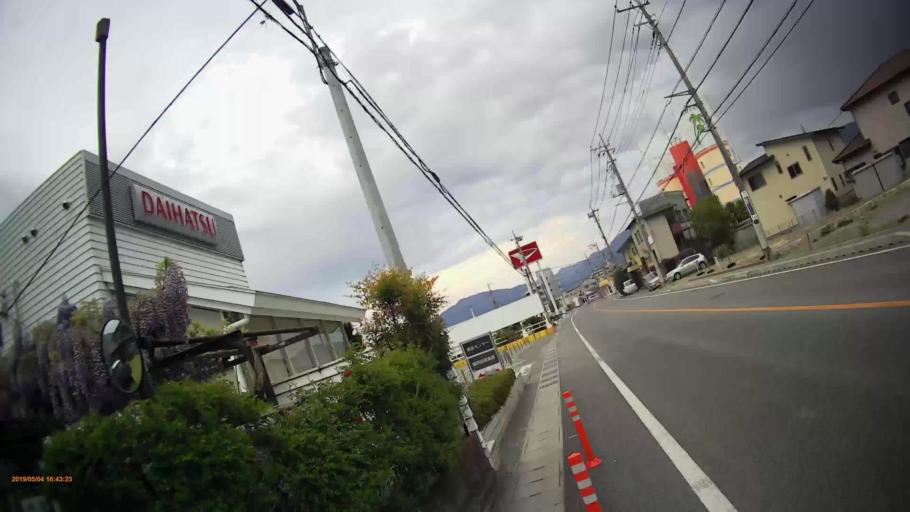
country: JP
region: Yamanashi
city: Isawa
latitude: 35.6558
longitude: 138.6071
